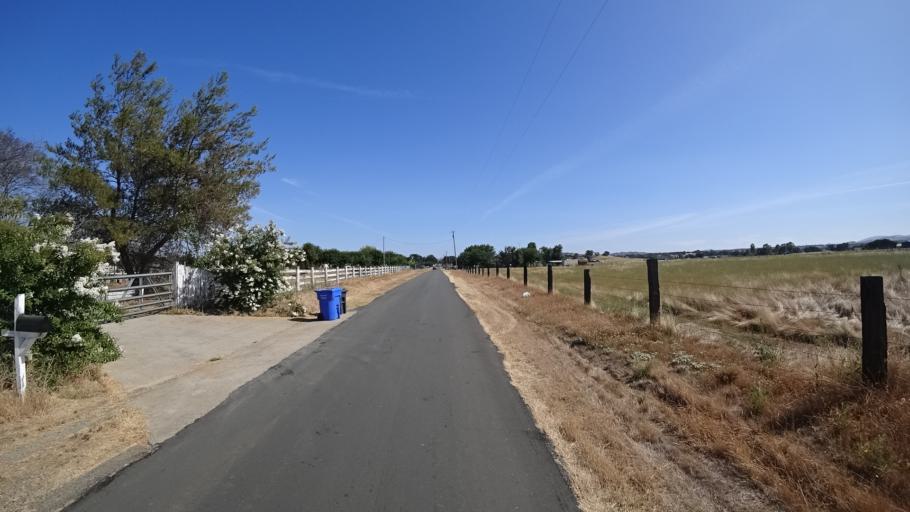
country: US
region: California
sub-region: Calaveras County
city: Rancho Calaveras
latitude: 38.0910
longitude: -120.9083
